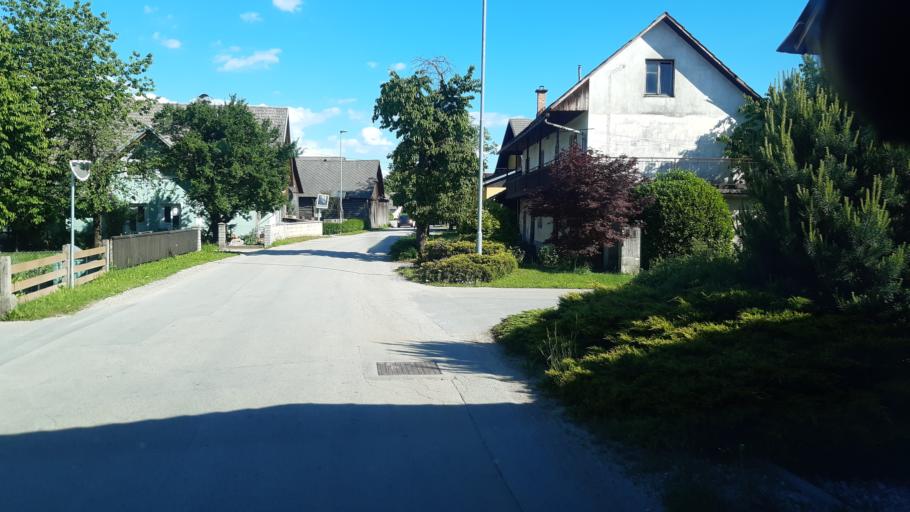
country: SI
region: Sencur
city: Hrastje
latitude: 46.2119
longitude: 14.3865
